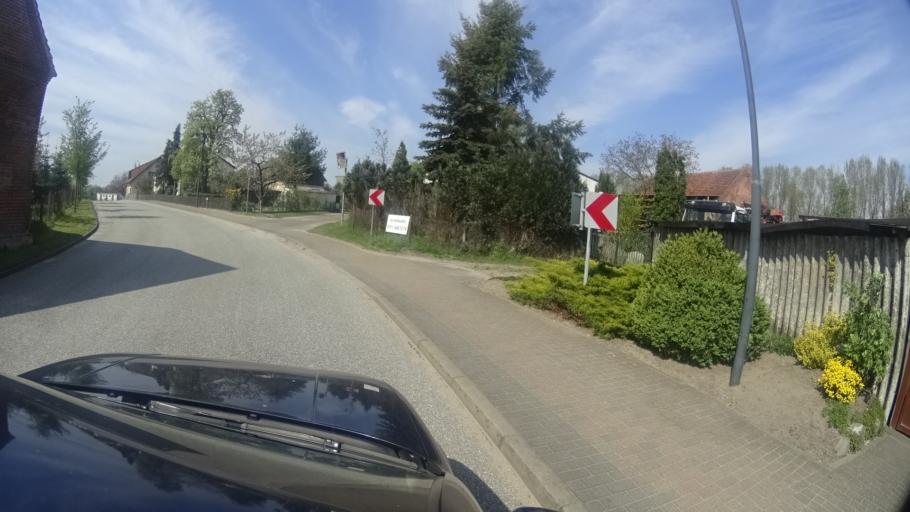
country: DE
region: Brandenburg
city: Dreetz
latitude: 52.7410
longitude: 12.4893
